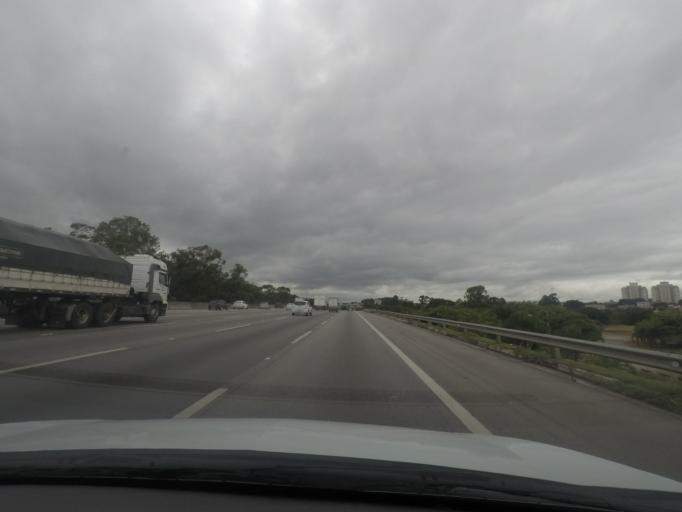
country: BR
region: Sao Paulo
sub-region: Guarulhos
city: Guarulhos
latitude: -23.4955
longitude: -46.5207
